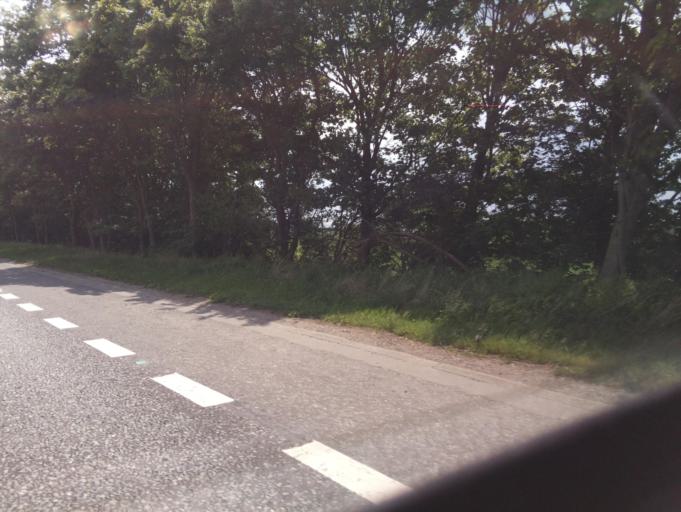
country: GB
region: England
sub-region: North Yorkshire
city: Thirsk
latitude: 54.3150
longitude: -1.3387
